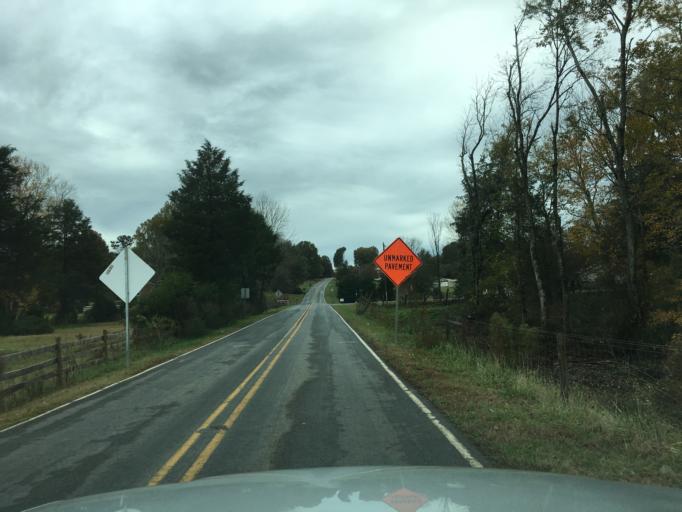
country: US
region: North Carolina
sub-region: Catawba County
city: Maiden
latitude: 35.6024
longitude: -81.2405
